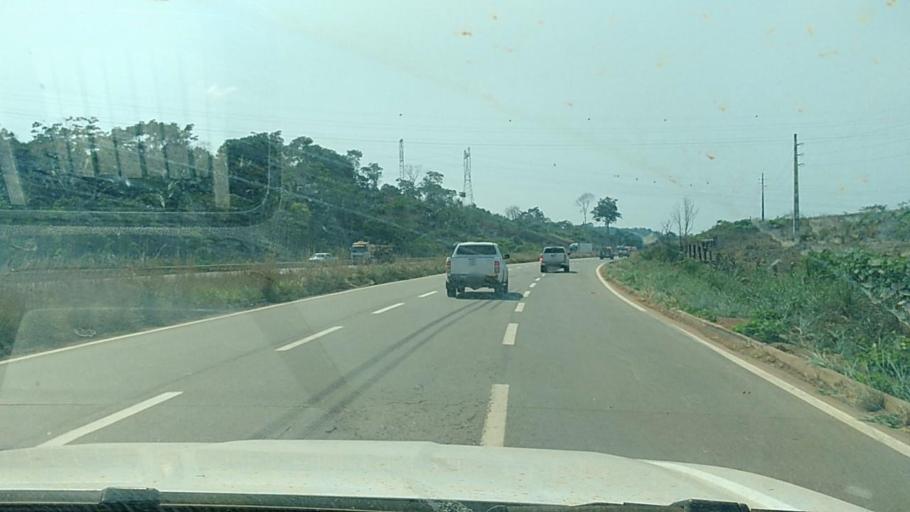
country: BR
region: Rondonia
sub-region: Porto Velho
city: Porto Velho
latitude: -8.7751
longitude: -63.4829
